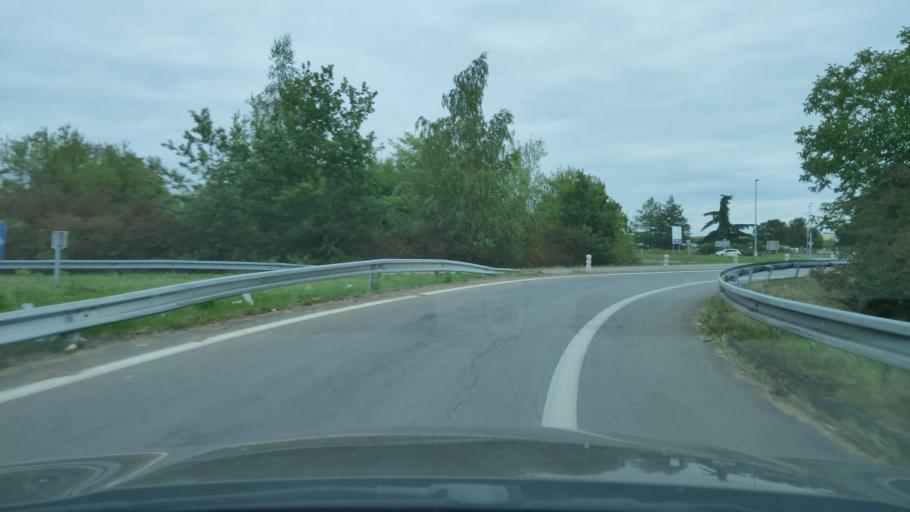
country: FR
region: Lorraine
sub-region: Departement de la Moselle
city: Maizieres-les-Metz
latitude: 49.2039
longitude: 6.1474
